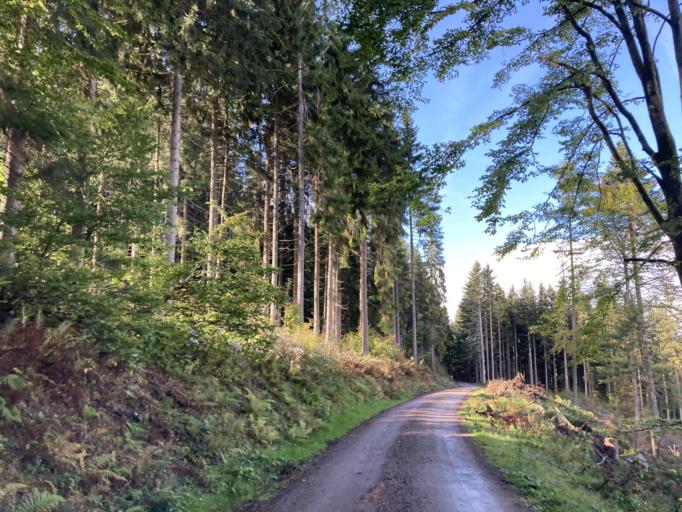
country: DE
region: Baden-Wuerttemberg
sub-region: Freiburg Region
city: Triberg im Schwarzwald
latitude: 48.1016
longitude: 8.2620
